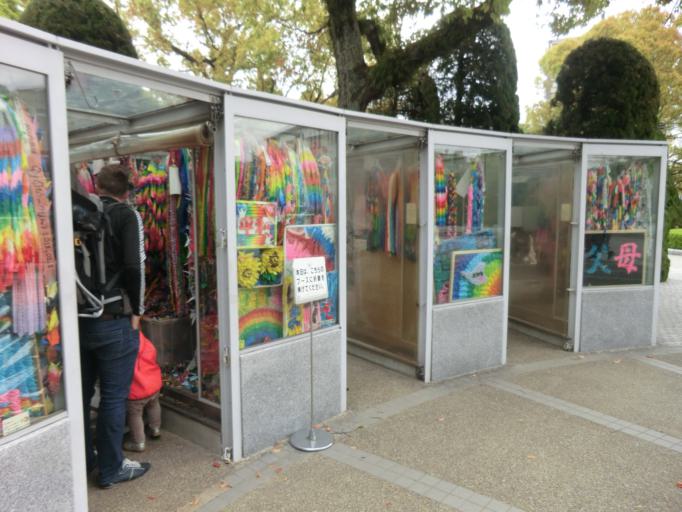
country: JP
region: Hiroshima
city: Hiroshima-shi
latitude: 34.3941
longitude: 132.4527
